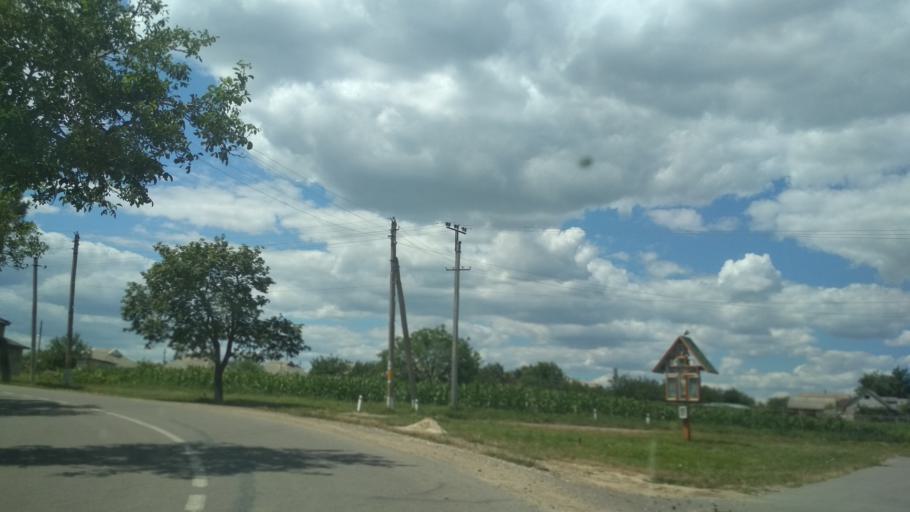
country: MD
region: Criuleni
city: Criuleni
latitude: 47.1781
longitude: 29.2032
